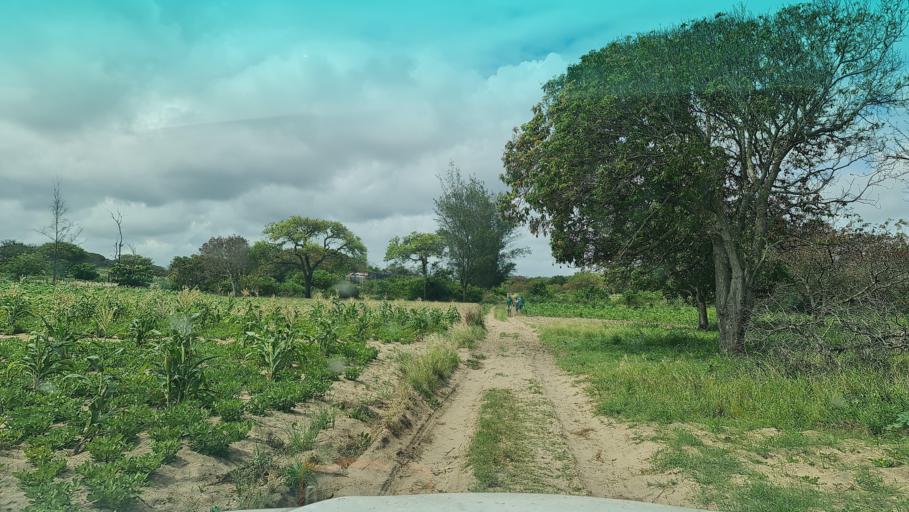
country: EG
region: Aswan
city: Idfu
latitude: 25.3974
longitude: 33.0278
